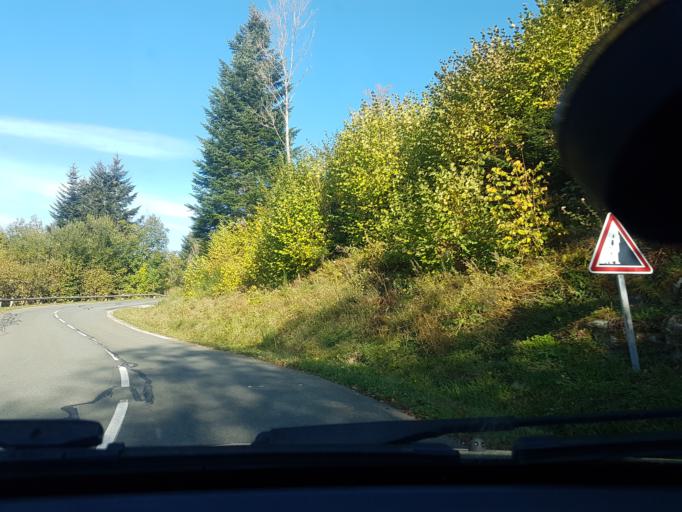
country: FR
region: Franche-Comte
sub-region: Departement de la Haute-Saone
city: Plancher-les-Mines
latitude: 47.7787
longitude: 6.7685
